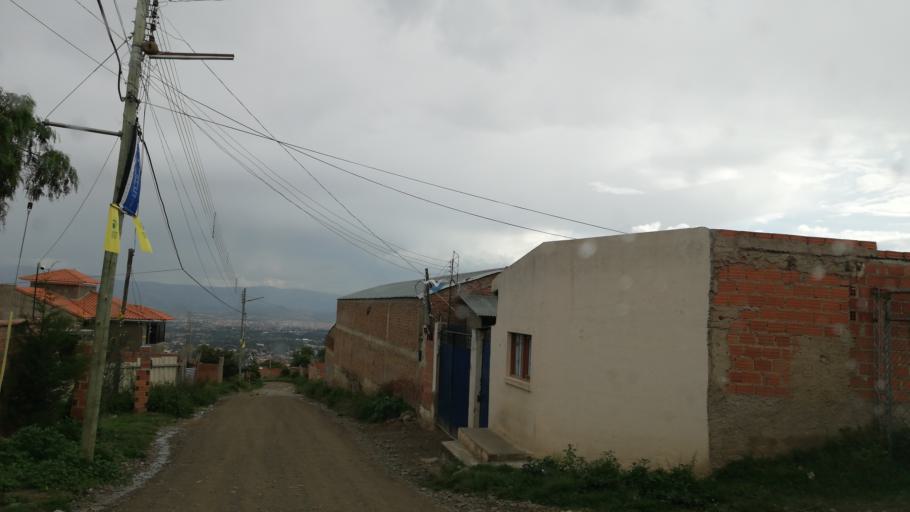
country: BO
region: Cochabamba
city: Cochabamba
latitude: -17.3276
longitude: -66.1924
